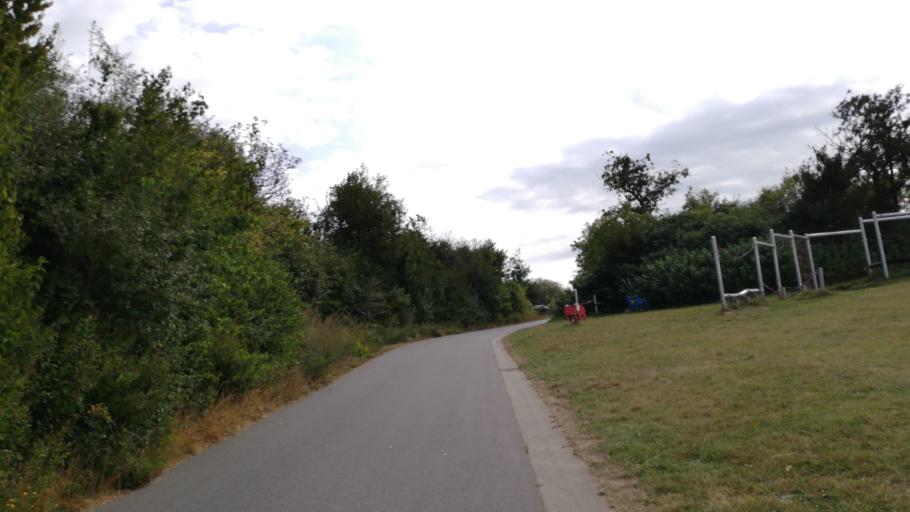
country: DE
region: Schleswig-Holstein
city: Tolk
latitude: 54.5754
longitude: 9.6306
